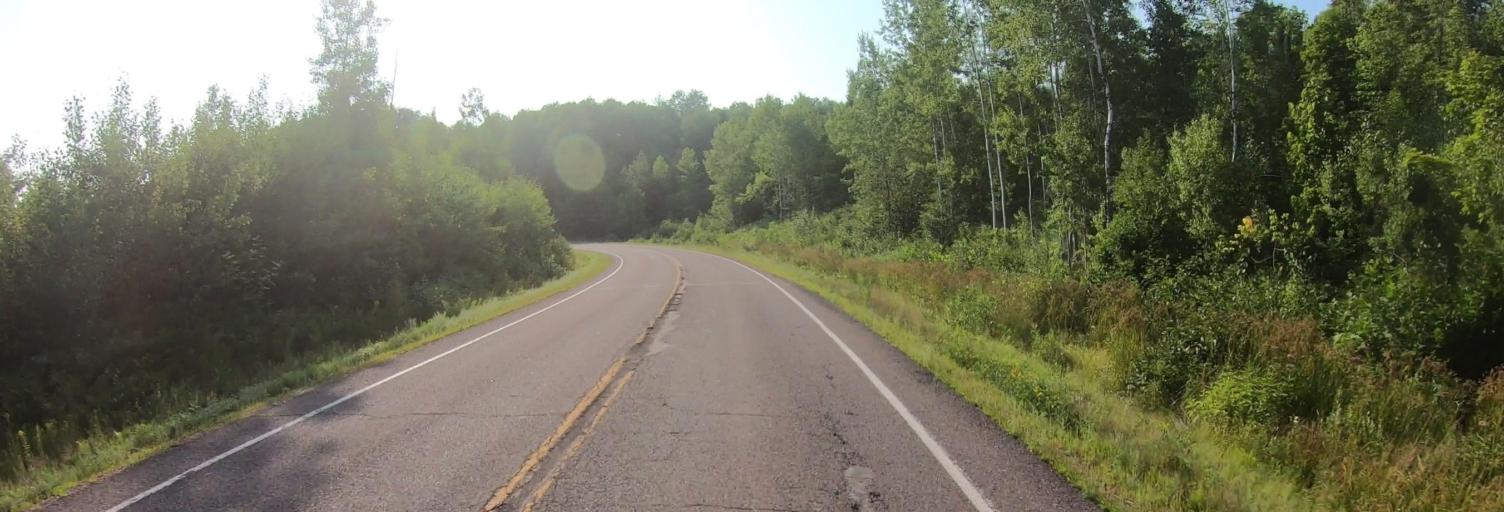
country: US
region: Wisconsin
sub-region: Ashland County
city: Ashland
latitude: 46.3199
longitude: -90.6769
